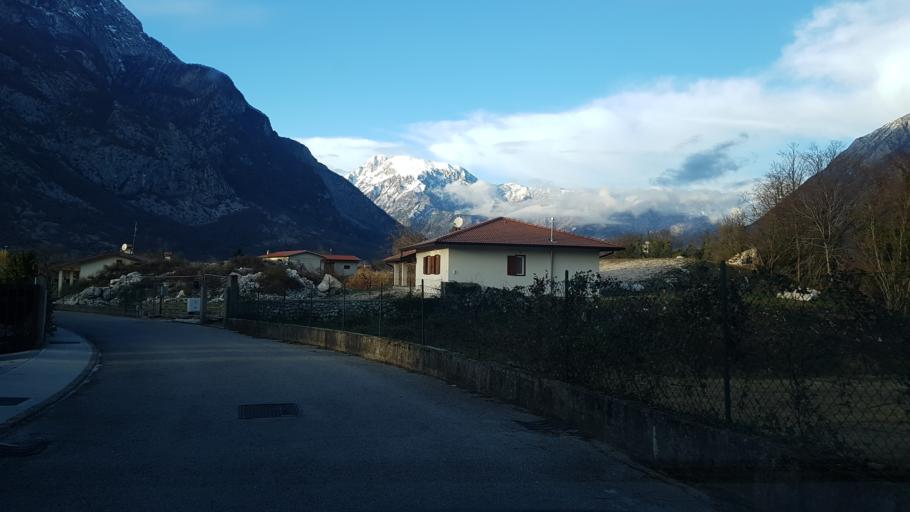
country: IT
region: Friuli Venezia Giulia
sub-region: Provincia di Udine
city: Venzone
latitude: 46.3272
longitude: 13.1404
